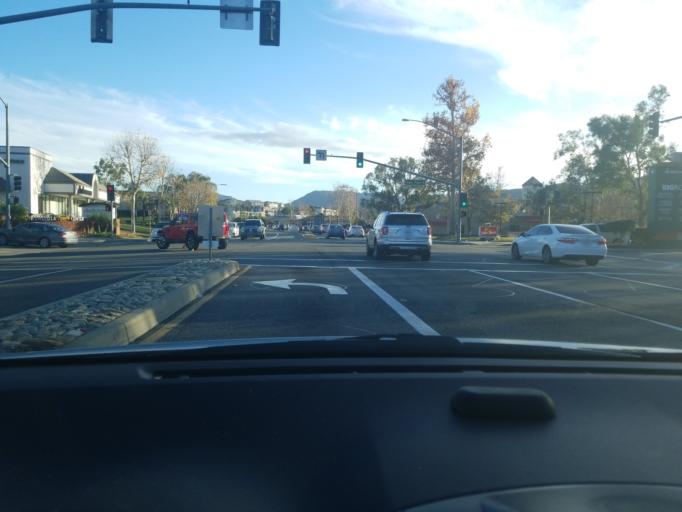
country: US
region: California
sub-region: Riverside County
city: Temecula
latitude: 33.5059
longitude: -117.1501
